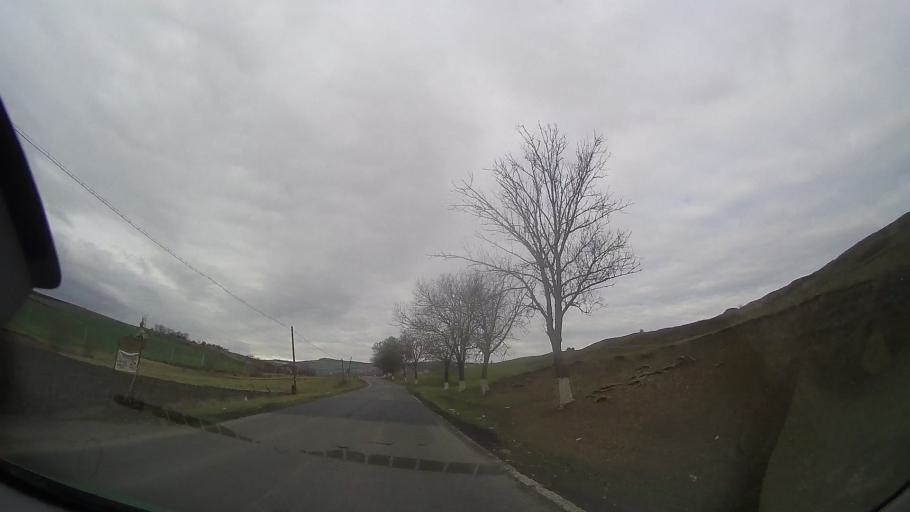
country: RO
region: Bistrita-Nasaud
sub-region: Comuna Urmenis
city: Urmenis
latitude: 46.7612
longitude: 24.3829
